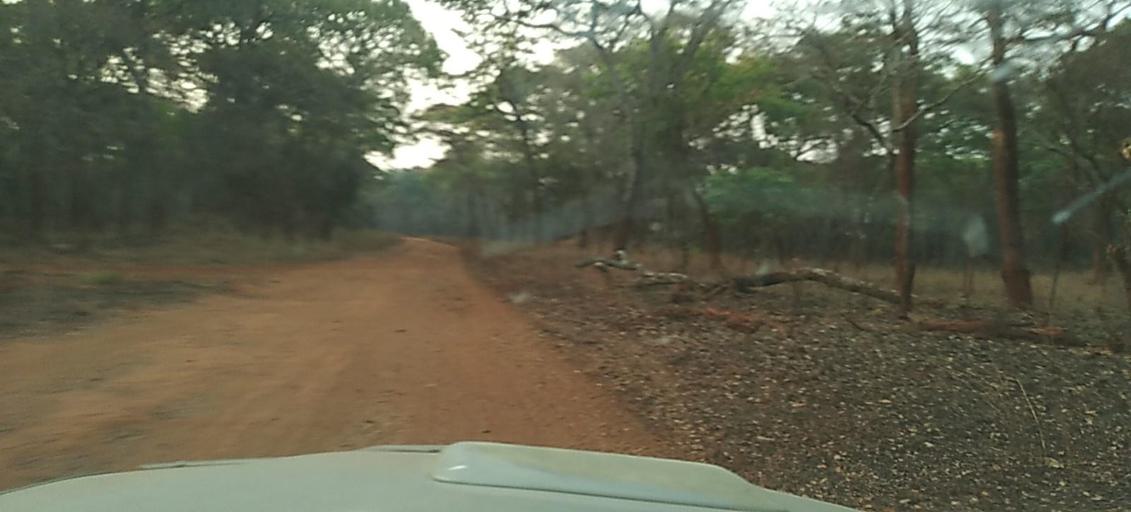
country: ZM
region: North-Western
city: Kasempa
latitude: -13.0944
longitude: 26.4011
